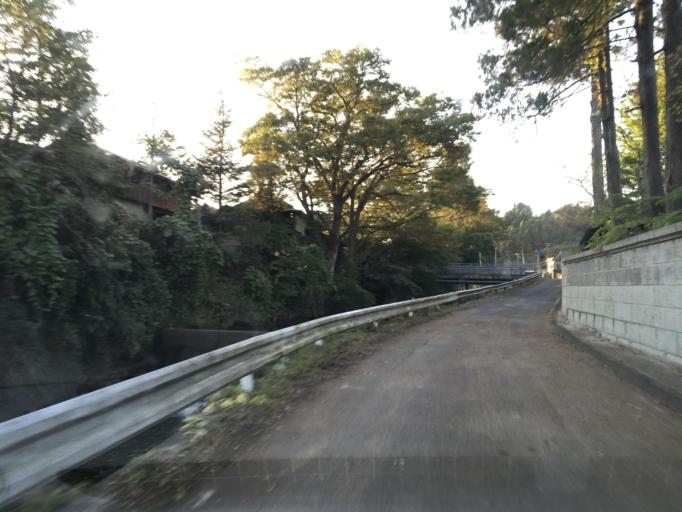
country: JP
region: Iwate
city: Ichinoseki
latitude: 38.8675
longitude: 141.1255
